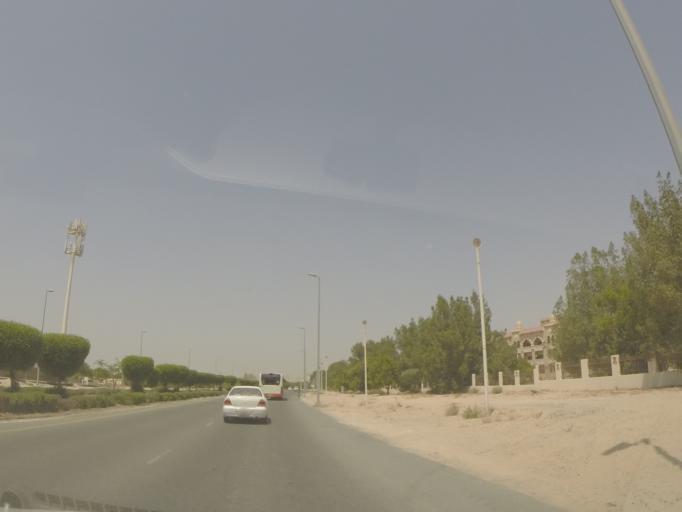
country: AE
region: Dubai
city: Dubai
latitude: 24.9909
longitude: 55.1809
